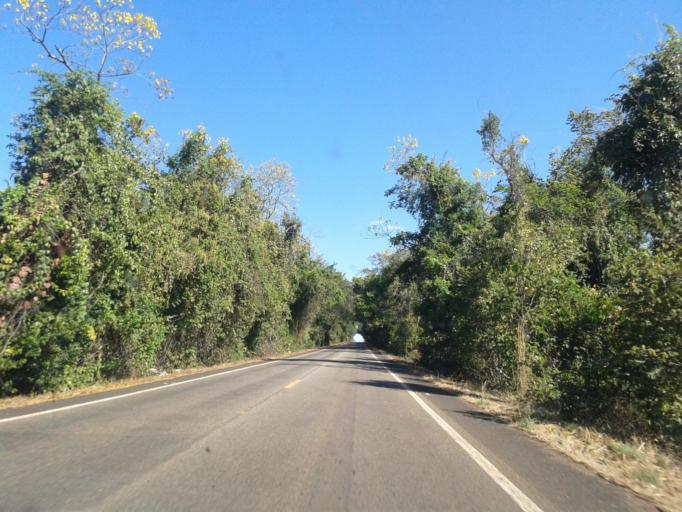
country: BR
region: Goias
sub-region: Crixas
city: Crixas
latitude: -14.0218
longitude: -50.3269
